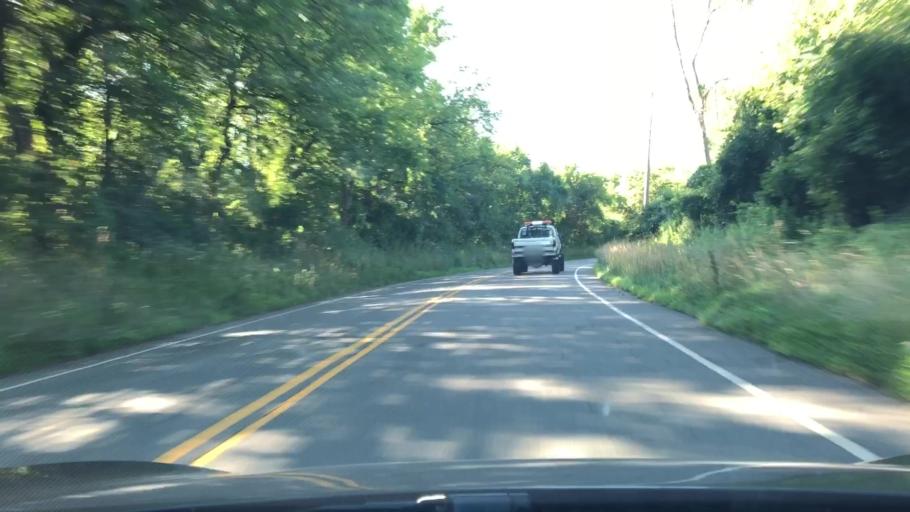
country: US
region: New Jersey
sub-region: Mercer County
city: Pennington
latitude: 40.3170
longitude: -74.8154
